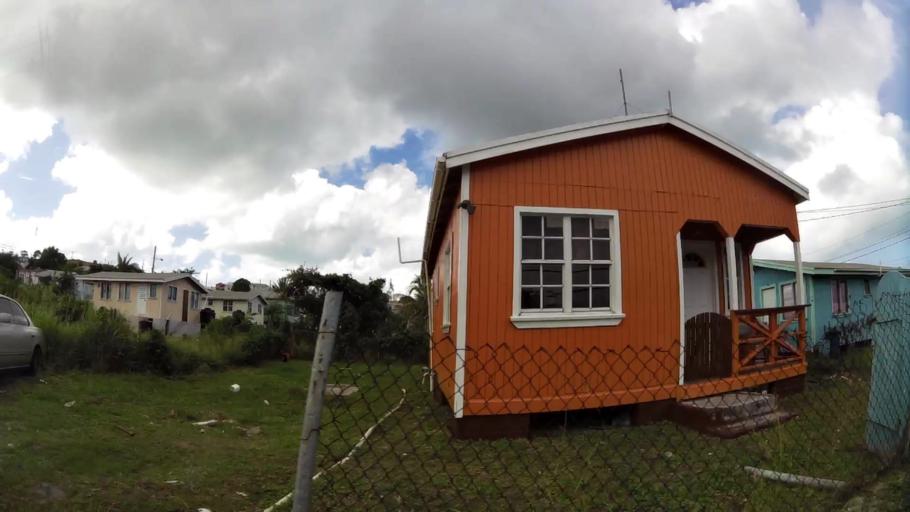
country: AG
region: Saint John
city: Saint John's
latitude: 17.1104
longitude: -61.8545
